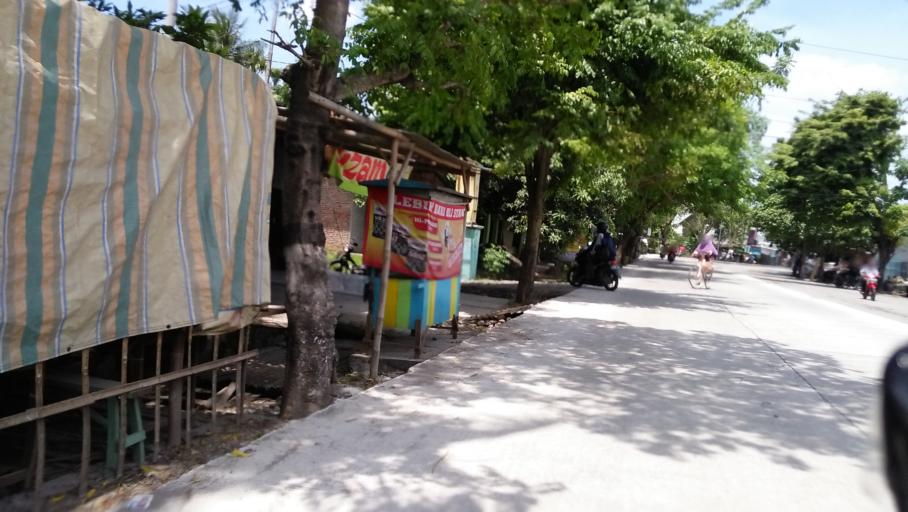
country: ID
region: Central Java
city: Mranggen
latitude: -6.9807
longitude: 110.4800
